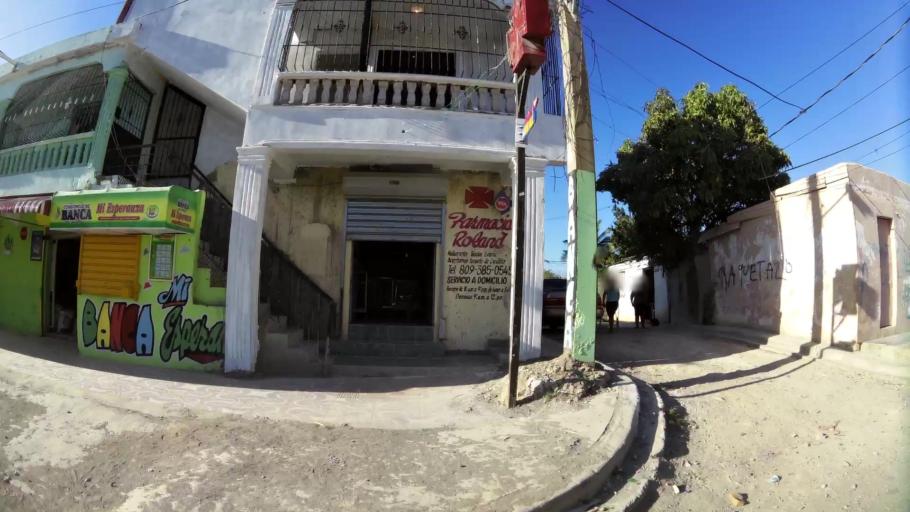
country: DO
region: Santo Domingo
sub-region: Santo Domingo
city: Santo Domingo Este
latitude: 18.4788
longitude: -69.8204
